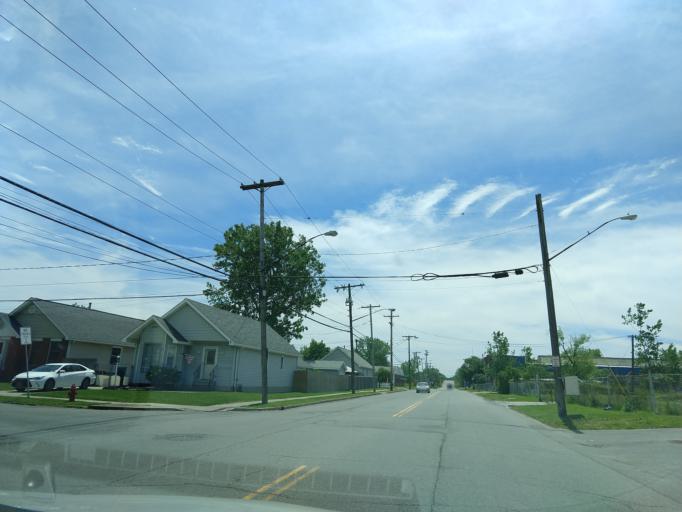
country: US
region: New York
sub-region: Erie County
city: Lackawanna
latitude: 42.8428
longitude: -78.8324
